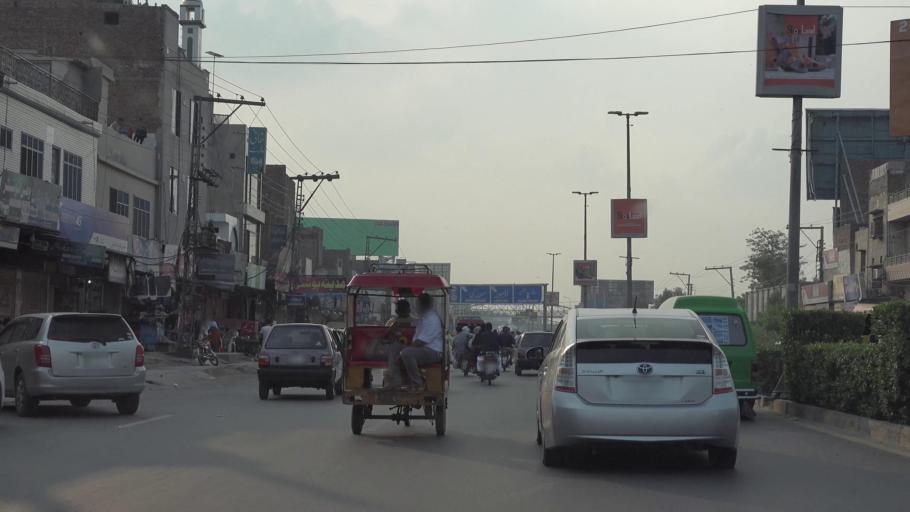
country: PK
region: Punjab
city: Faisalabad
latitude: 31.4180
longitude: 73.1069
